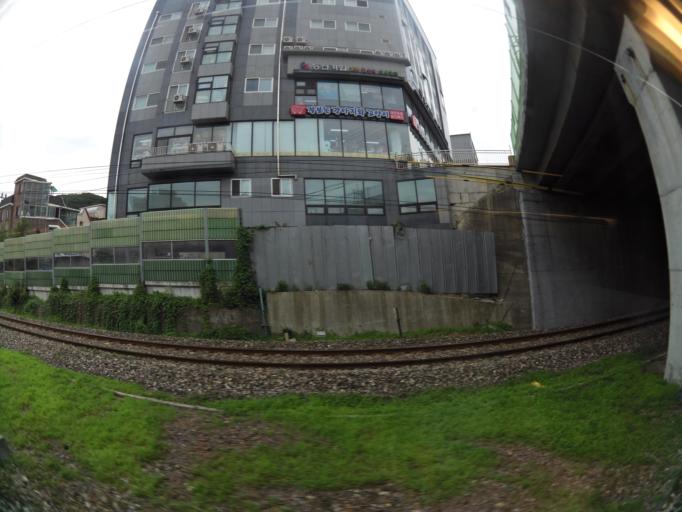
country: KR
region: Gyeonggi-do
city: Anyang-si
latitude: 37.3829
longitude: 126.9360
